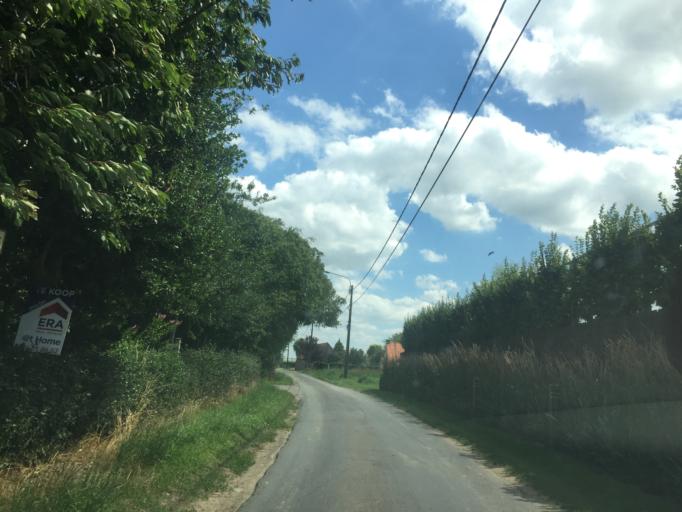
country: BE
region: Flanders
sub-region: Provincie West-Vlaanderen
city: Staden
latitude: 50.9990
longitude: 3.0014
